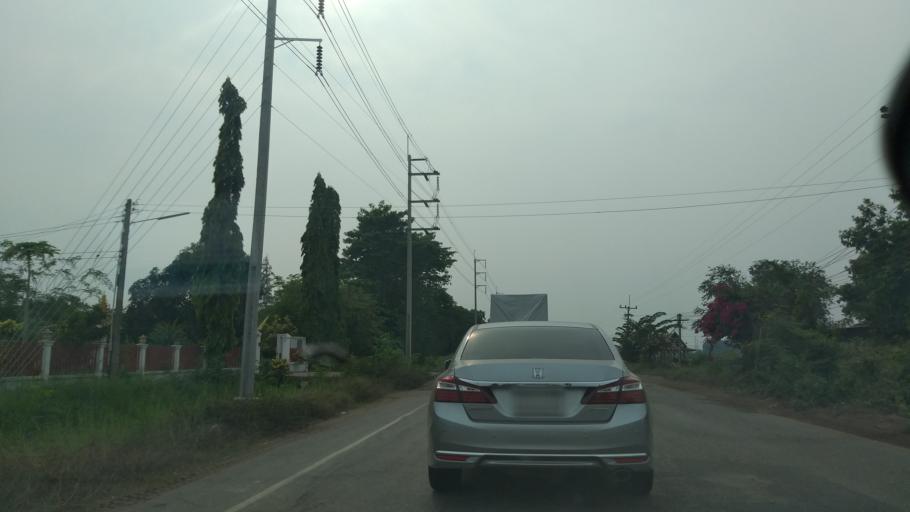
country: TH
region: Chachoengsao
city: Ban Pho
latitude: 13.5983
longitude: 101.1814
